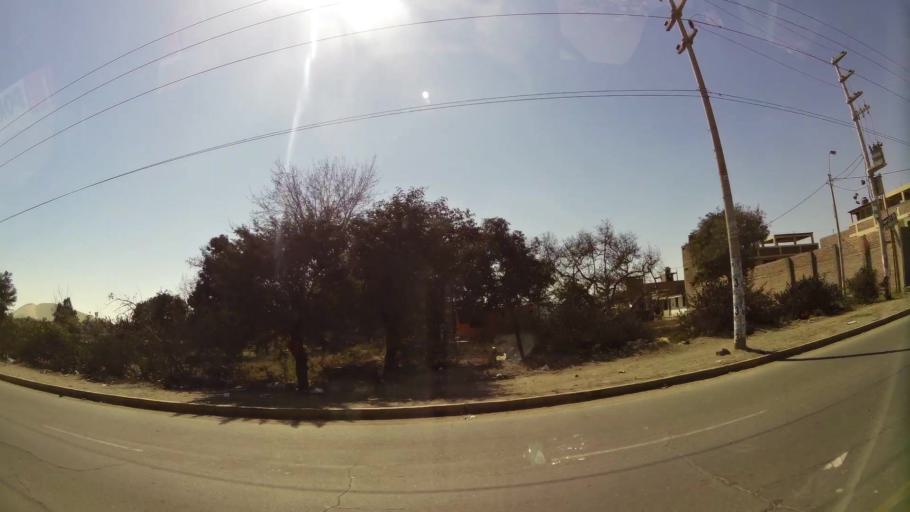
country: PE
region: Ica
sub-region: Provincia de Ica
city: Ica
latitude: -14.0595
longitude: -75.7149
